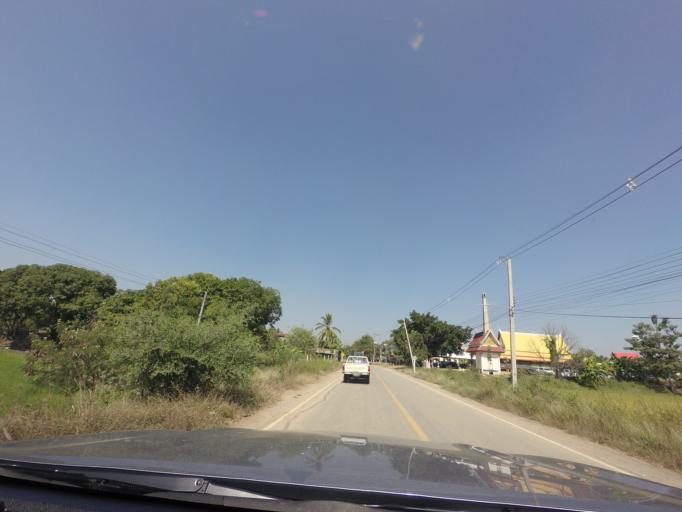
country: TH
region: Sukhothai
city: Si Samrong
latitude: 17.1669
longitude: 99.7700
